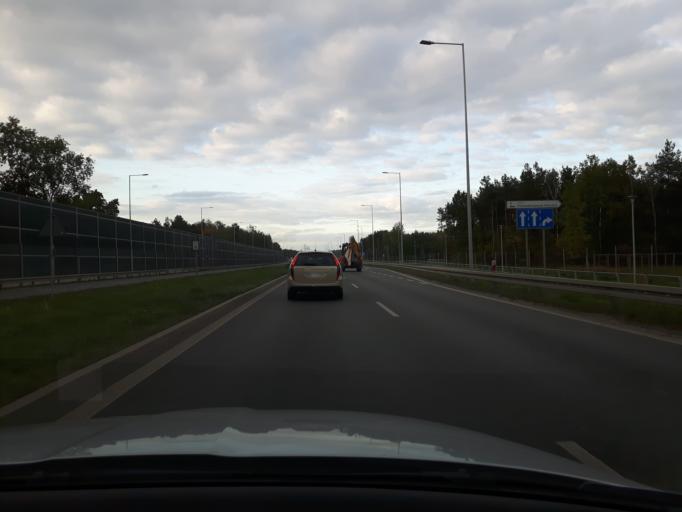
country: PL
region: Masovian Voivodeship
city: Zielonka
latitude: 52.2874
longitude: 21.1399
